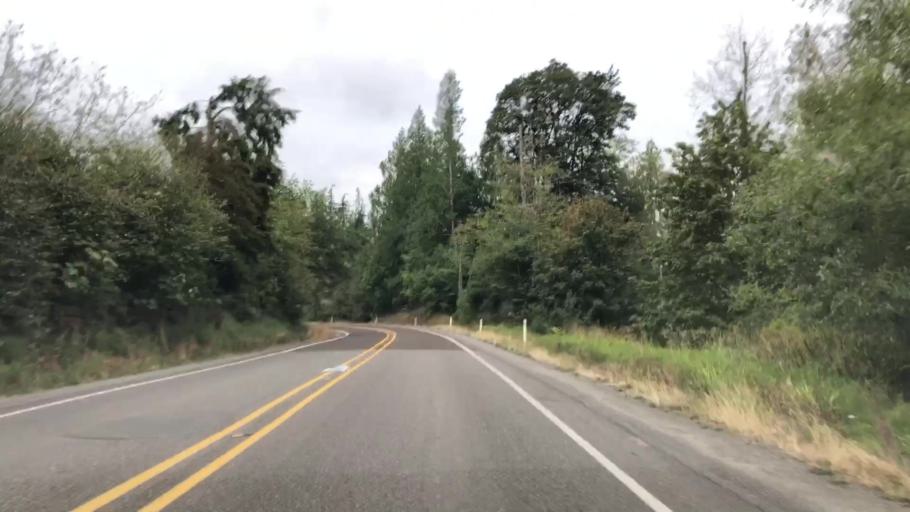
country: US
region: Washington
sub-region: Kitsap County
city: Navy Yard City
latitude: 47.5280
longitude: -122.7235
